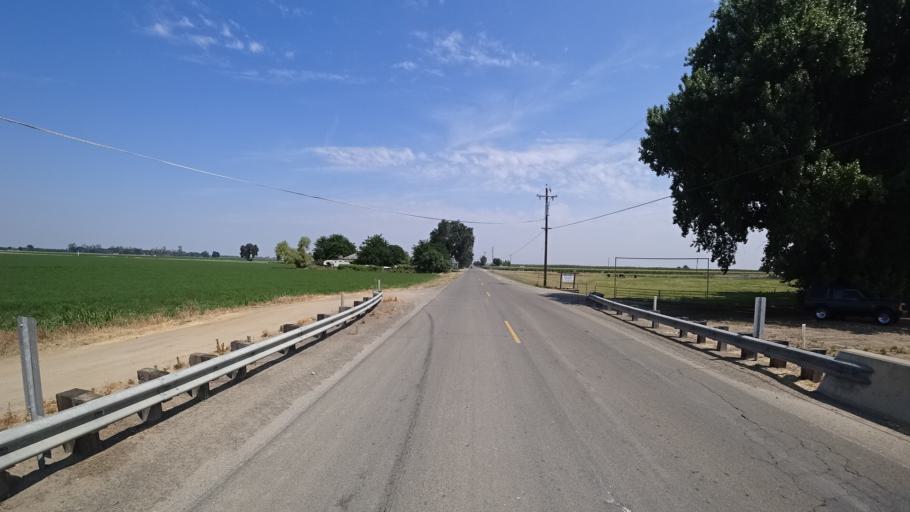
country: US
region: California
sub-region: Kings County
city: Armona
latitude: 36.3624
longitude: -119.7450
